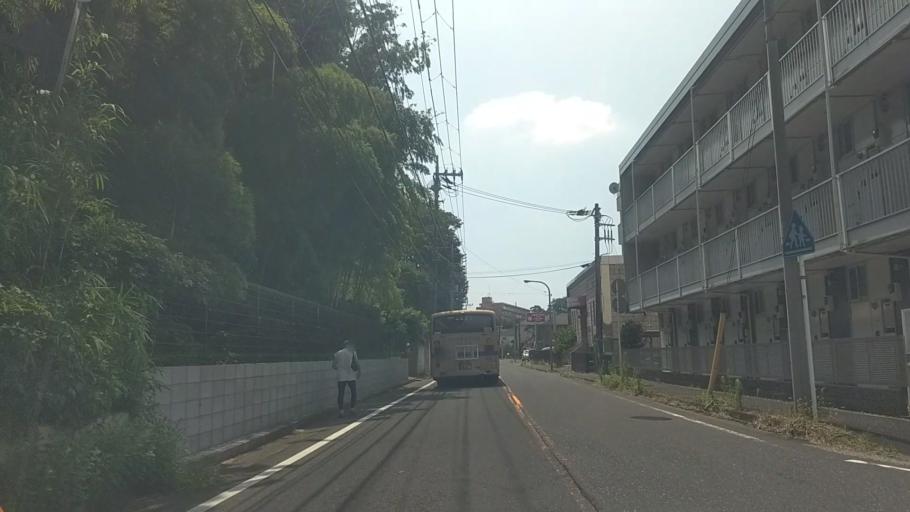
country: JP
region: Kanagawa
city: Yokohama
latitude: 35.5033
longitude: 139.6537
